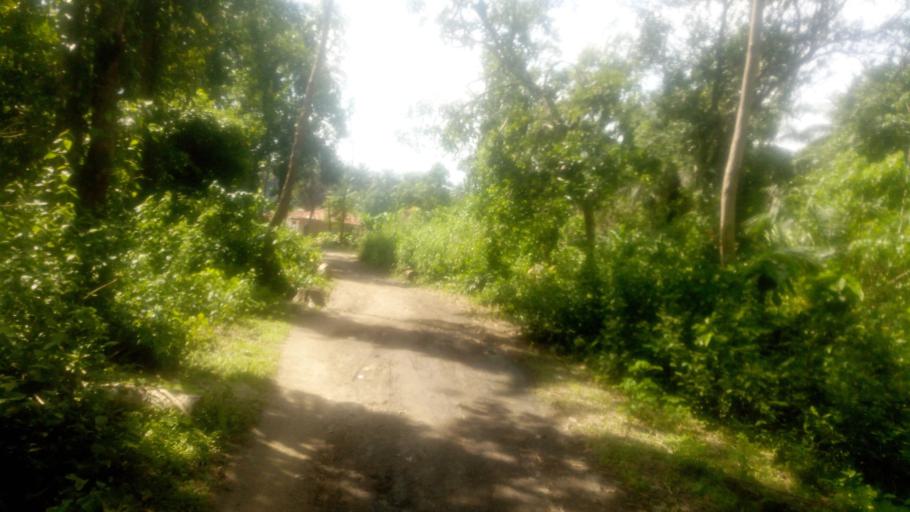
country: SL
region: Northern Province
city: Magburaka
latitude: 8.6619
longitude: -12.0697
